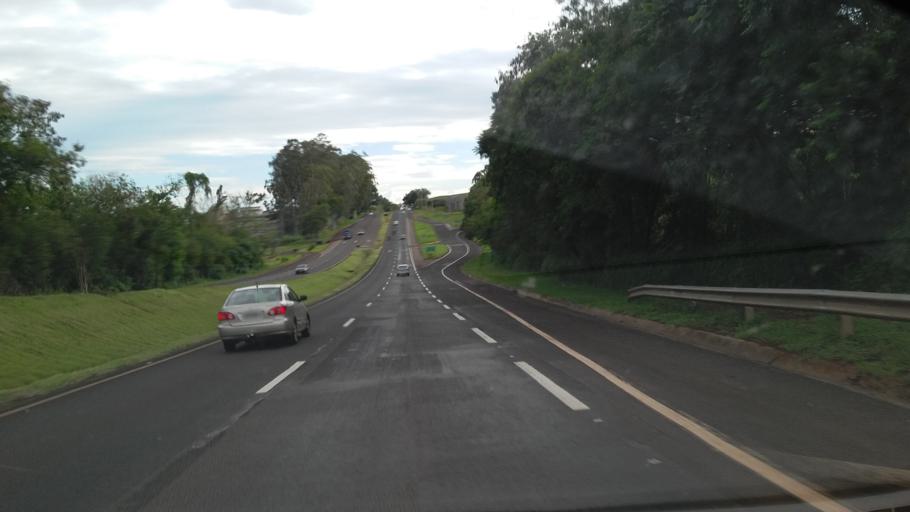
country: BR
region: Parana
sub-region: Paicandu
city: Paicandu
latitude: -23.5195
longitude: -52.0288
